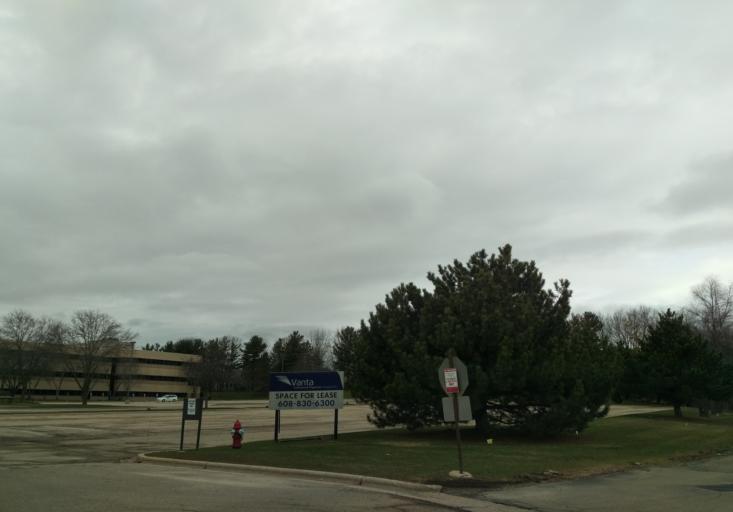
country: US
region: Wisconsin
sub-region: Dane County
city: Middleton
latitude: 43.0621
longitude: -89.5052
